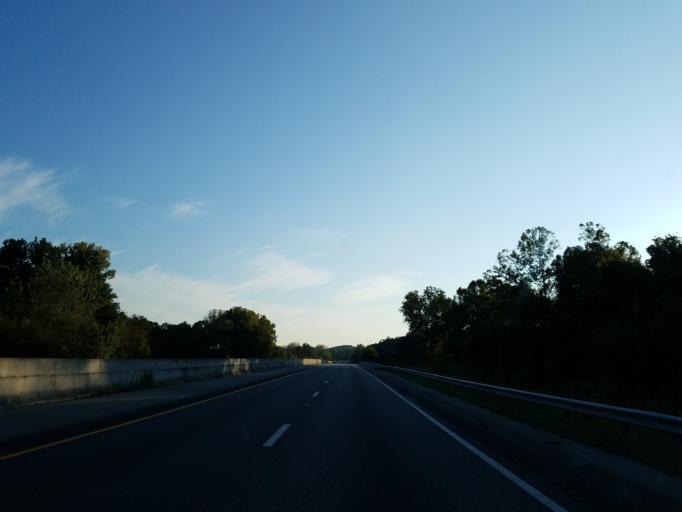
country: US
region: South Carolina
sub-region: Cherokee County
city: Blacksburg
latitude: 35.1192
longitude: -81.5750
